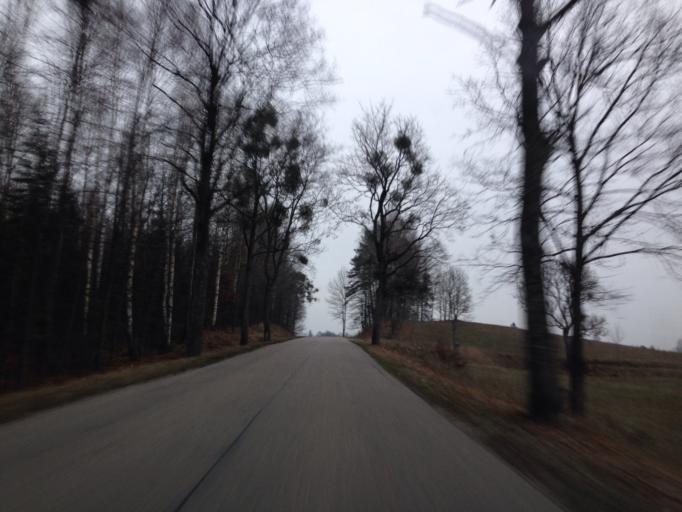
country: PL
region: Warmian-Masurian Voivodeship
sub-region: Powiat olsztynski
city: Biskupiec
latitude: 53.8733
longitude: 21.0067
